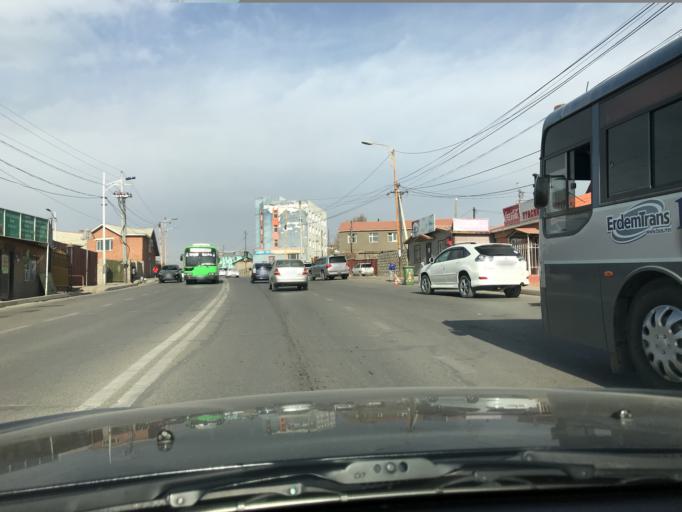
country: MN
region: Ulaanbaatar
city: Ulaanbaatar
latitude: 47.9332
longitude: 106.8870
